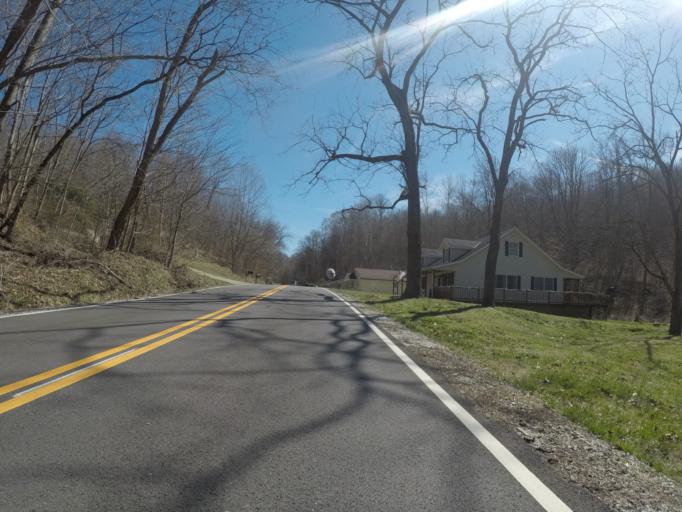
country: US
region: Ohio
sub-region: Lawrence County
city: South Point
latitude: 38.4623
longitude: -82.5589
